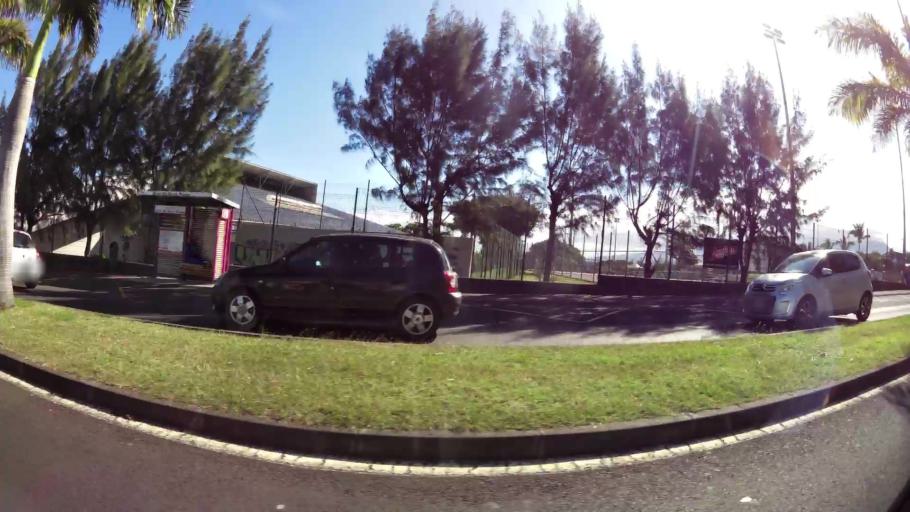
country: RE
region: Reunion
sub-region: Reunion
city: Saint-Pierre
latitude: -21.3336
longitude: 55.4713
